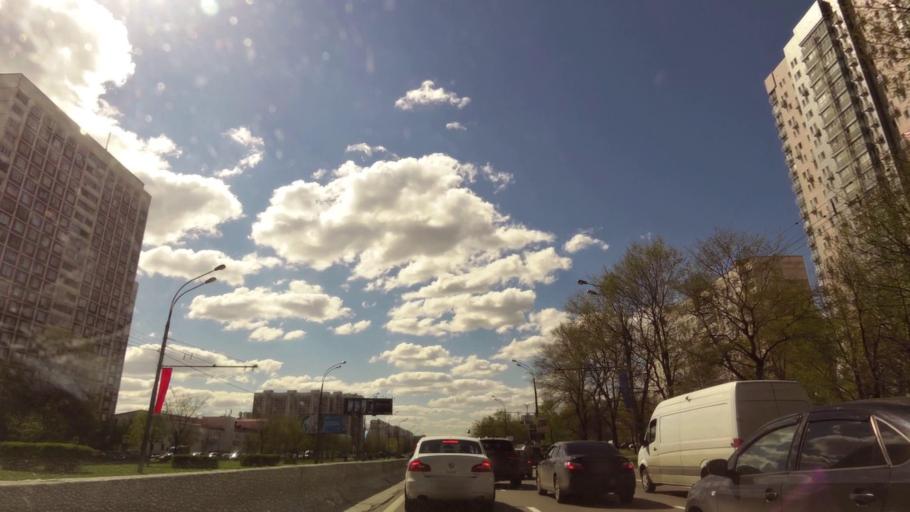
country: RU
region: Moscow
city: Lianozovo
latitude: 55.8918
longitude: 37.5867
